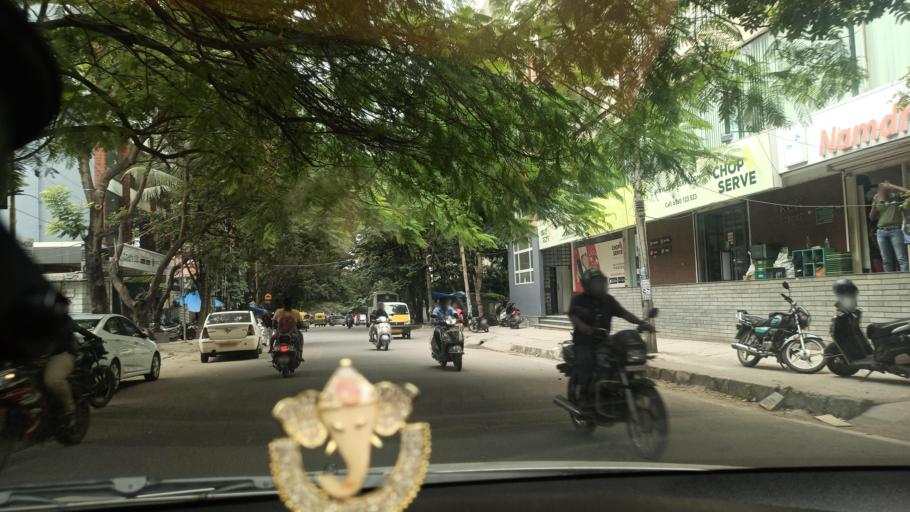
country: IN
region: Karnataka
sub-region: Bangalore Urban
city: Bangalore
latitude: 12.9175
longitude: 77.6493
